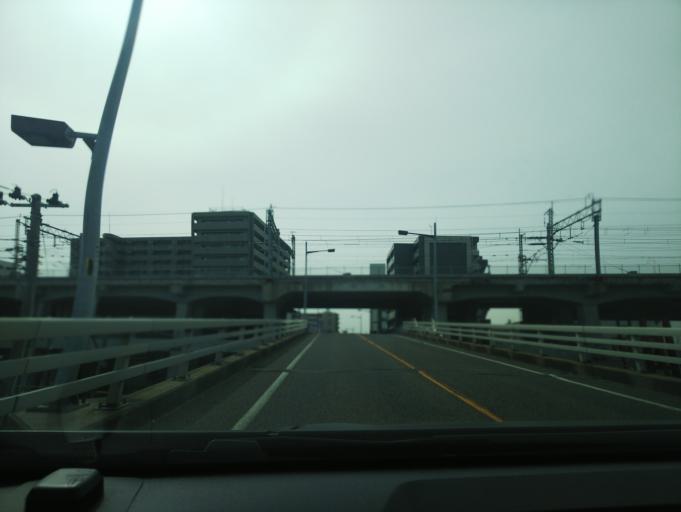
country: JP
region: Niigata
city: Niigata-shi
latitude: 37.9138
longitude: 139.0667
